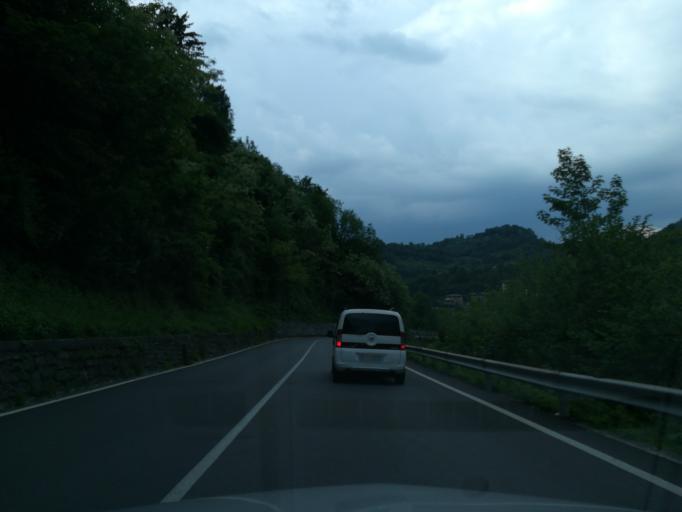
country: IT
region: Lombardy
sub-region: Provincia di Bergamo
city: Camoneone
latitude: 45.7871
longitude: 9.5722
